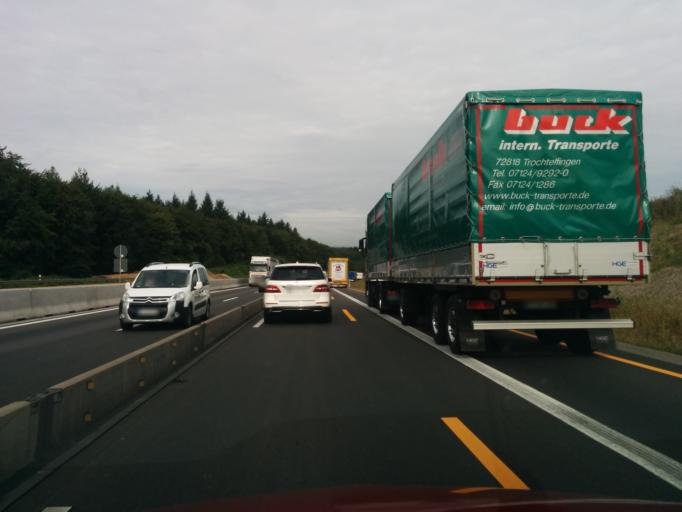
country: DE
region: Baden-Wuerttemberg
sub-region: Karlsruhe Region
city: Konigsbach-Stein
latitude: 48.9204
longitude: 8.6088
